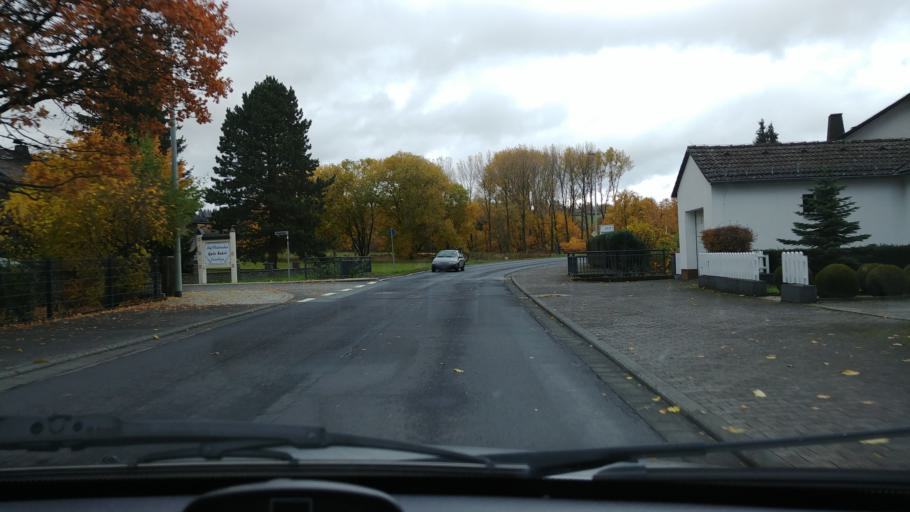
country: DE
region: Hesse
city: Mengerskirchen
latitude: 50.5681
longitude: 8.1563
